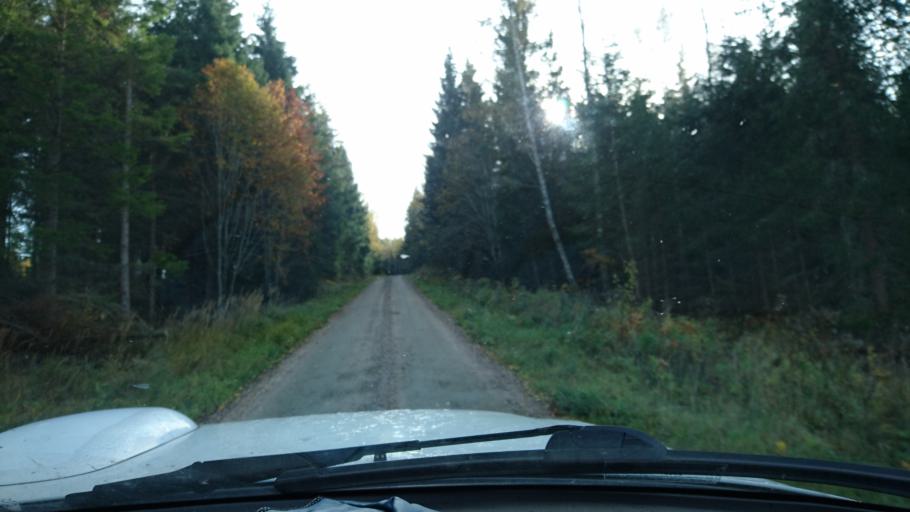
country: SE
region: Vaestra Goetaland
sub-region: Ulricehamns Kommun
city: Ulricehamn
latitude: 57.9528
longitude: 13.5271
